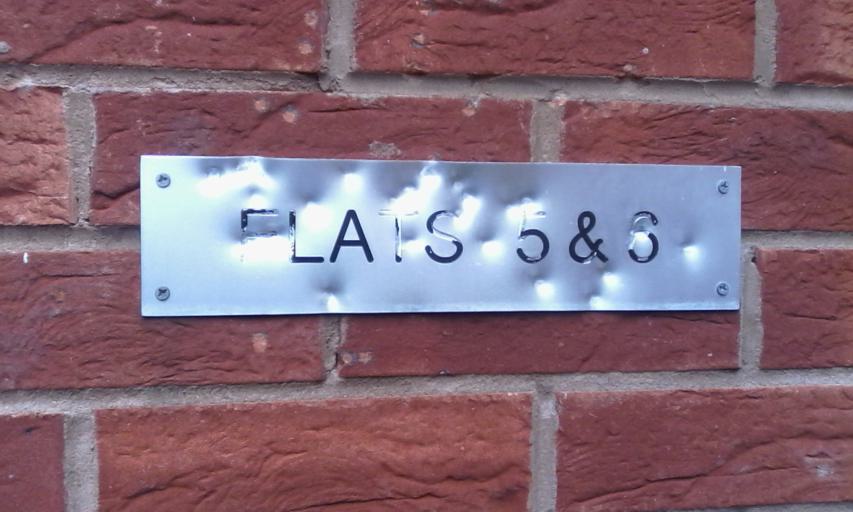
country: GB
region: England
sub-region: Nottinghamshire
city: Arnold
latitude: 52.9757
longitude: -1.1044
